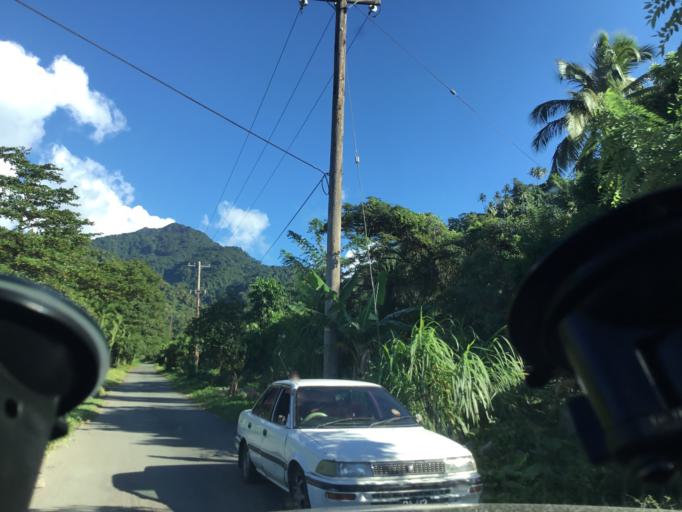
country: VC
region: Saint David
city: Chateaubelair
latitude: 13.3082
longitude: -61.2338
